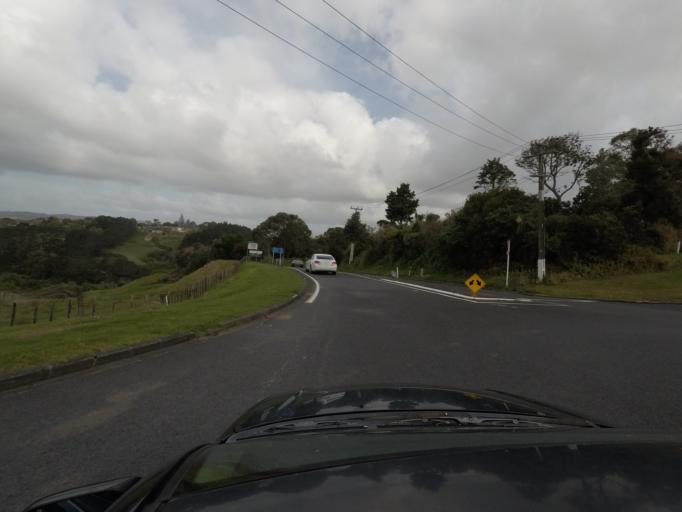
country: NZ
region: Auckland
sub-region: Auckland
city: Pakuranga
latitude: -36.9214
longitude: 174.9327
